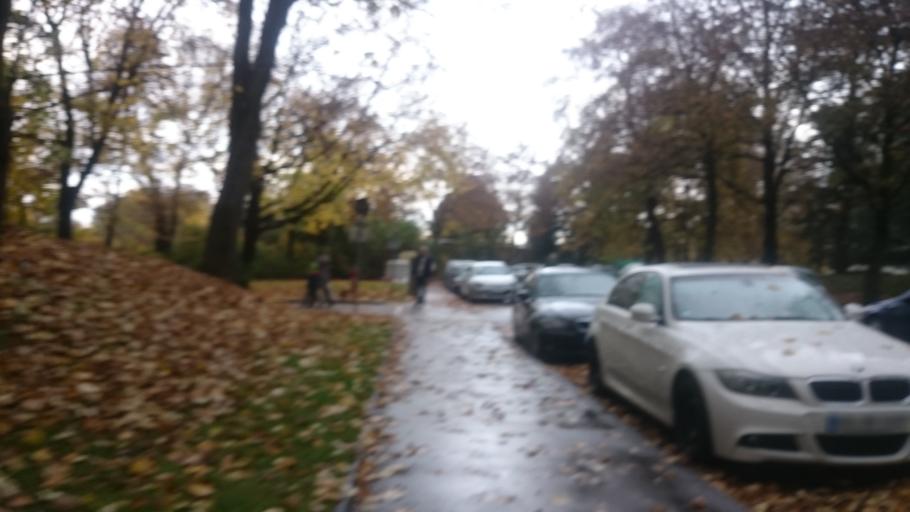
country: DE
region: Bavaria
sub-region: Swabia
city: Augsburg
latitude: 48.3562
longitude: 10.9221
